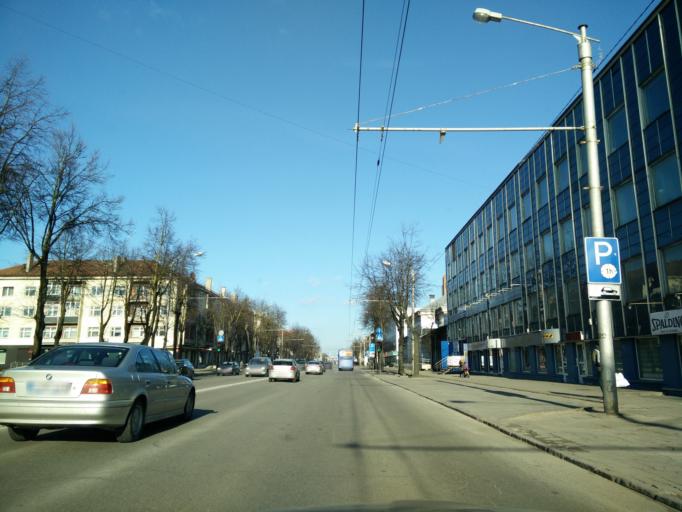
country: LT
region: Kauno apskritis
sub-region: Kaunas
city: Eiguliai
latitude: 54.9096
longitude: 23.9311
